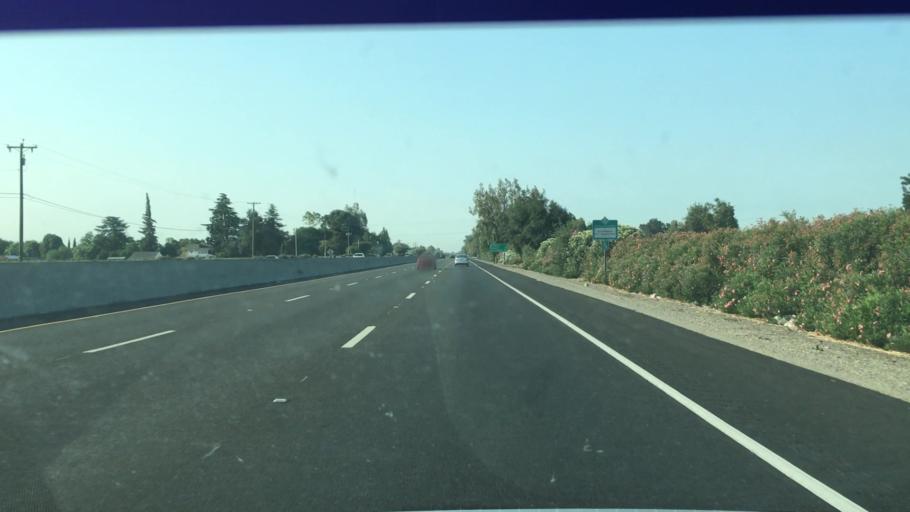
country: US
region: California
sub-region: San Joaquin County
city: Morada
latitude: 38.0836
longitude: -121.2601
